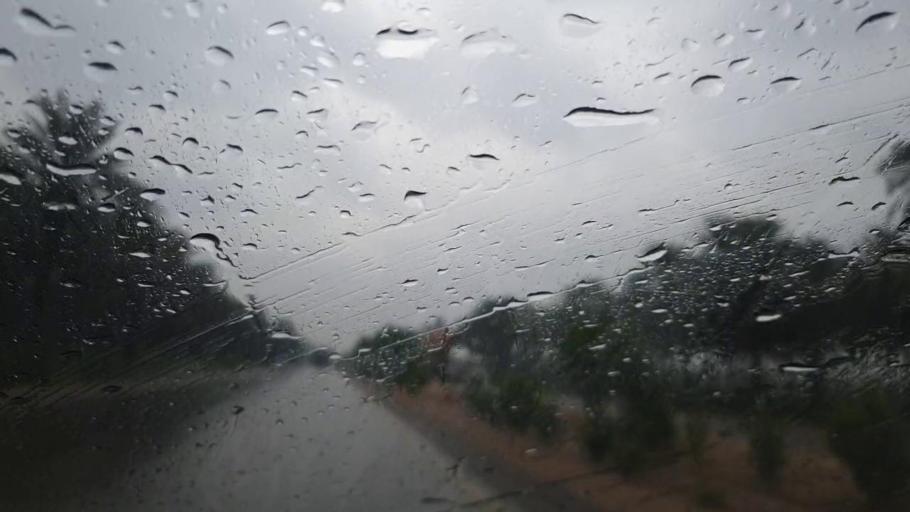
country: PK
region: Sindh
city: Khairpur
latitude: 27.5761
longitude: 68.7531
